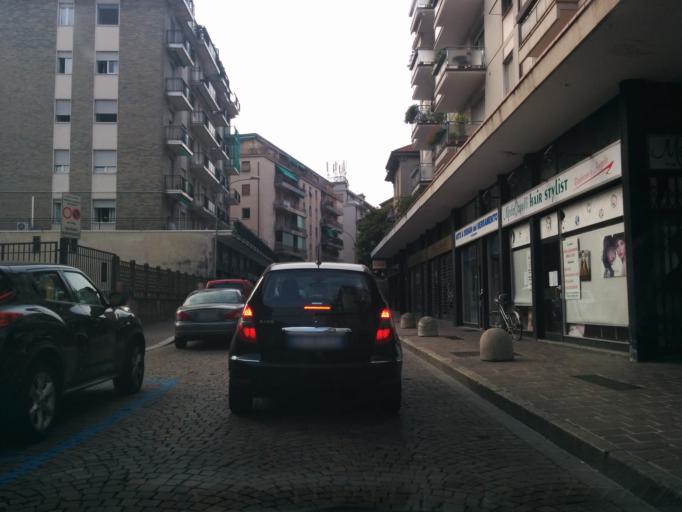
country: IT
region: Lombardy
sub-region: Provincia di Como
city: Como
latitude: 45.8062
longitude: 9.0881
